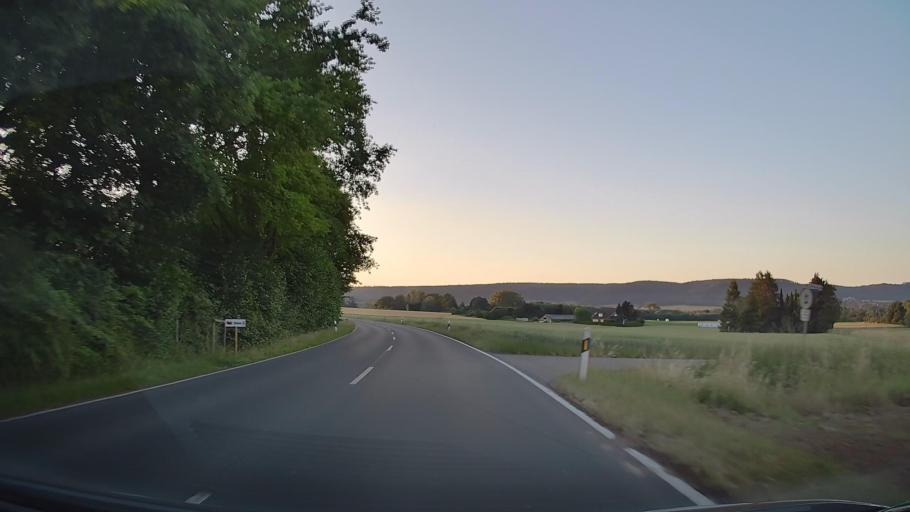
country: DE
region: North Rhine-Westphalia
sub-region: Regierungsbezirk Detmold
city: Lugde
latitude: 51.9698
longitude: 9.2351
